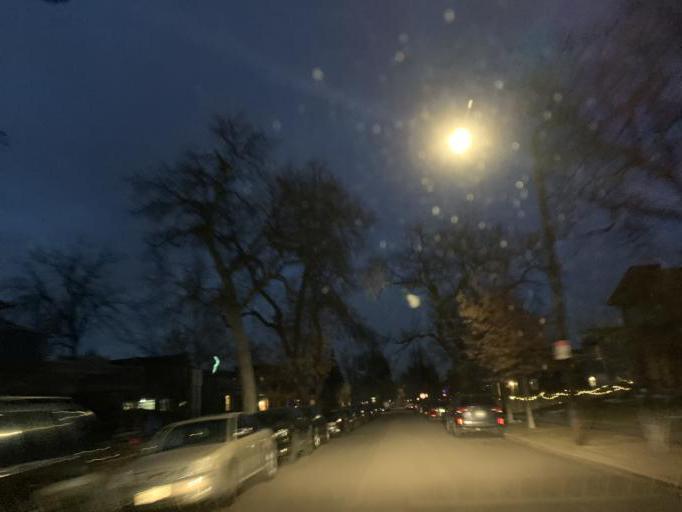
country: US
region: Colorado
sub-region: Jefferson County
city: Edgewater
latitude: 39.7737
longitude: -105.0474
